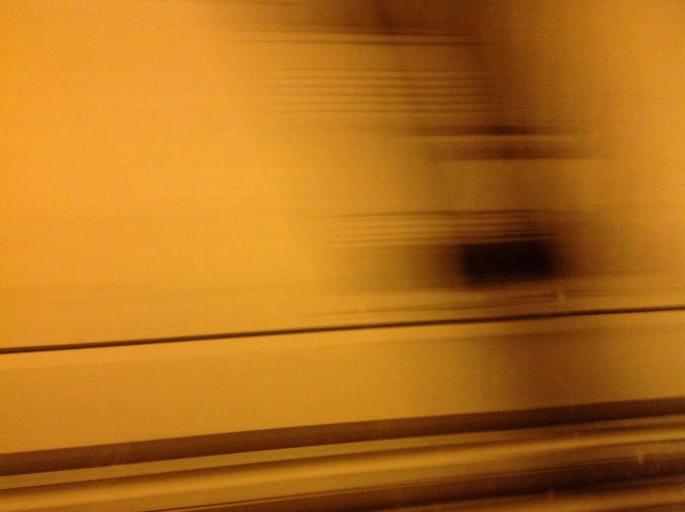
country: GR
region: Attica
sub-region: Nomarchia Athinas
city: Agia Paraskevi
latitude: 38.0011
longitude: 23.8314
